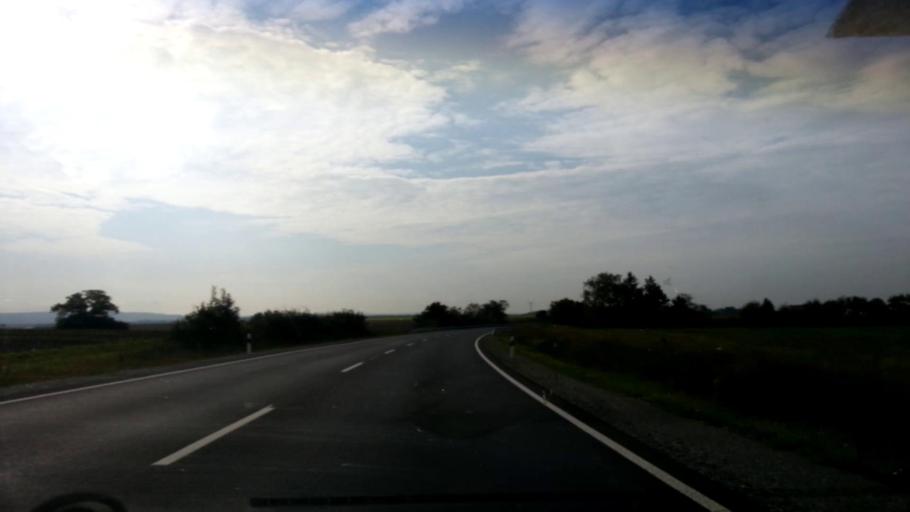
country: DE
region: Bavaria
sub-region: Regierungsbezirk Unterfranken
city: Gerolzhofen
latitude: 49.8748
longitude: 10.3611
